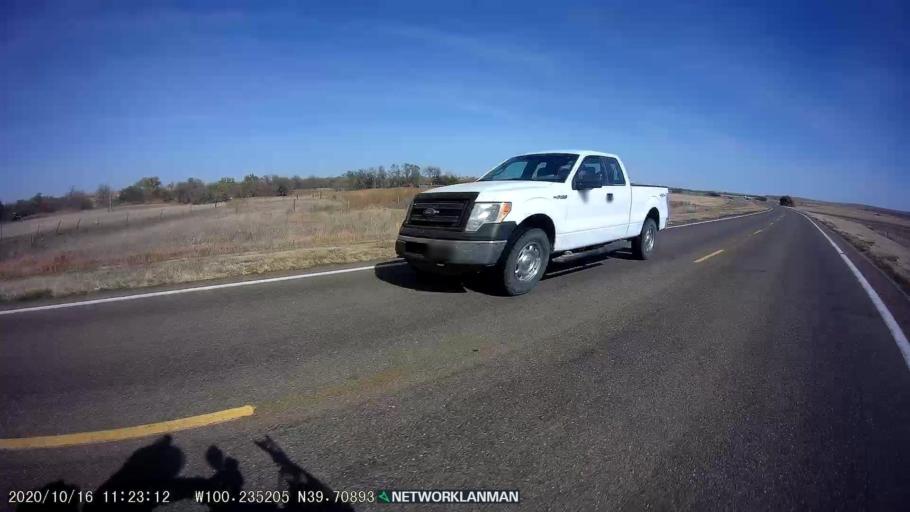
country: US
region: Kansas
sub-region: Decatur County
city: Oberlin
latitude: 39.7081
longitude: -100.2361
